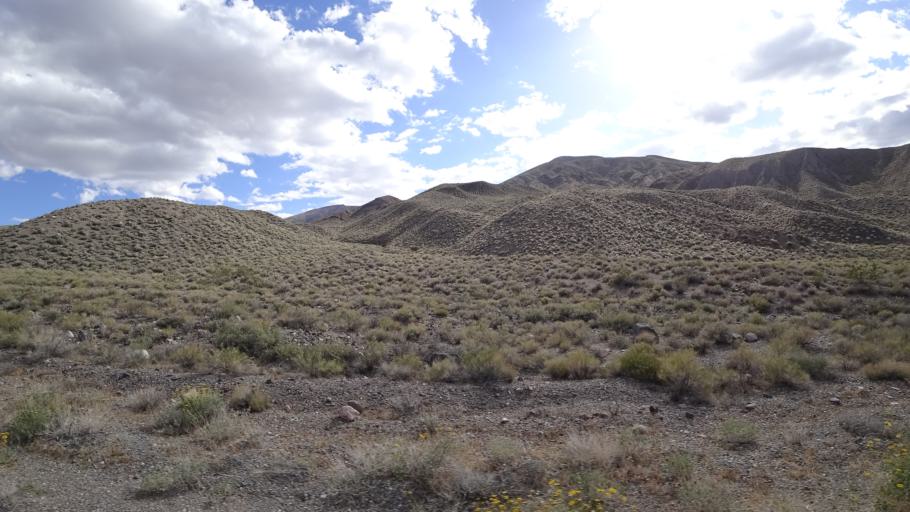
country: US
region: Nevada
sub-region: Nye County
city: Beatty
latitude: 36.4167
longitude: -117.1864
